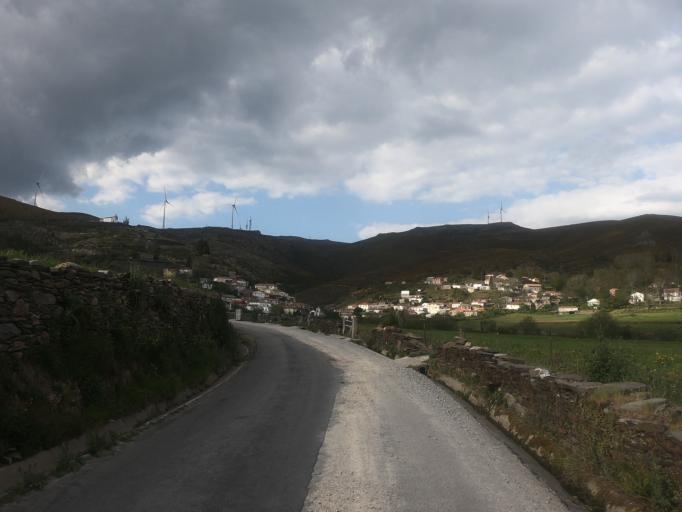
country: PT
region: Vila Real
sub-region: Vila Real
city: Vila Real
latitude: 41.3128
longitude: -7.8599
